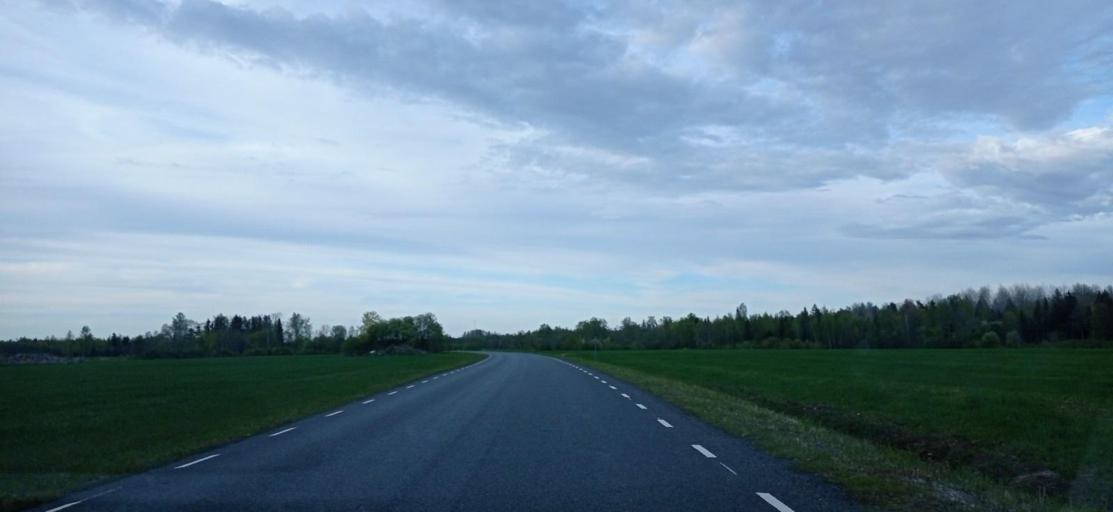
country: EE
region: Paernumaa
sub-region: Tootsi vald
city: Tootsi
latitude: 58.5464
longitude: 24.7738
